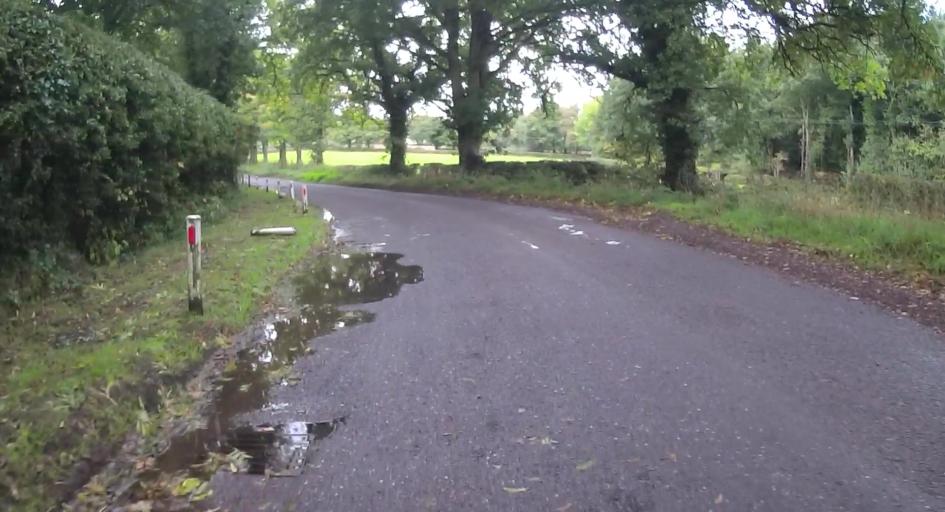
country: GB
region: England
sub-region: Hampshire
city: Tadley
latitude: 51.3224
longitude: -1.1555
